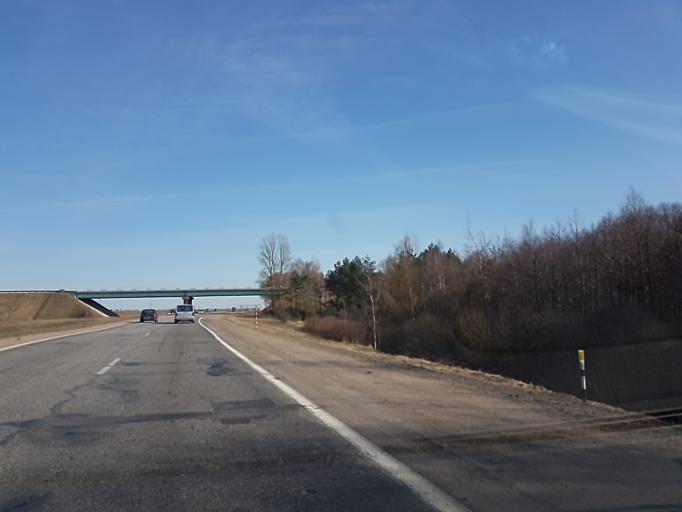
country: BY
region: Minsk
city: Dukora
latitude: 53.6607
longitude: 27.9457
